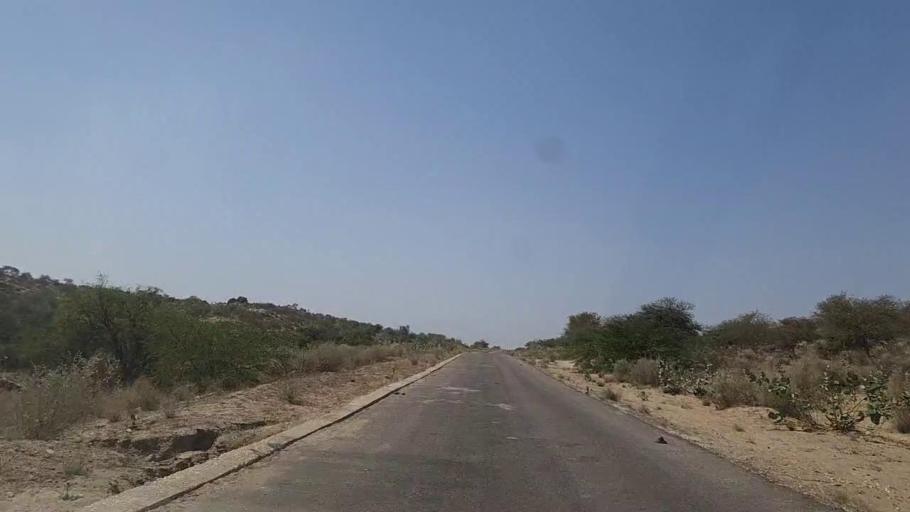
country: PK
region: Sindh
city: Diplo
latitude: 24.5714
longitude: 69.4751
